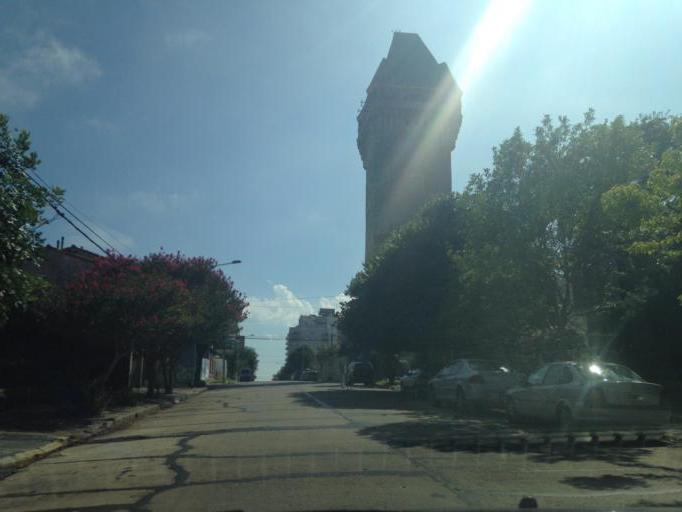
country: AR
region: Buenos Aires
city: Mar del Plata
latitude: -38.0137
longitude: -57.5359
